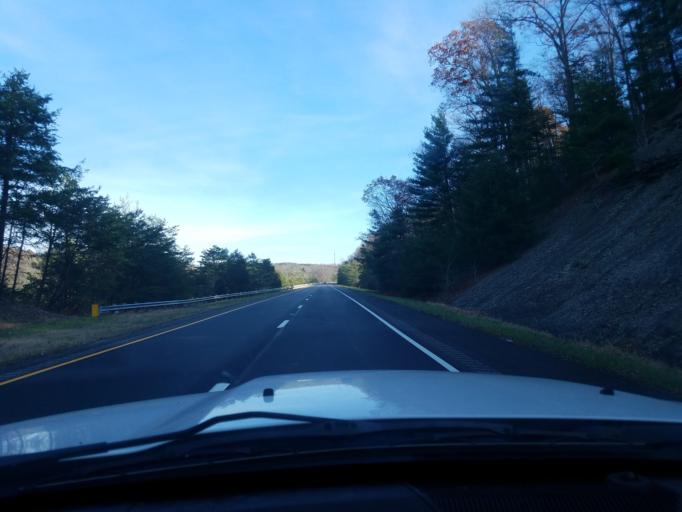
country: US
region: Ohio
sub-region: Adams County
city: Peebles
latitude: 39.0143
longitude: -83.2931
